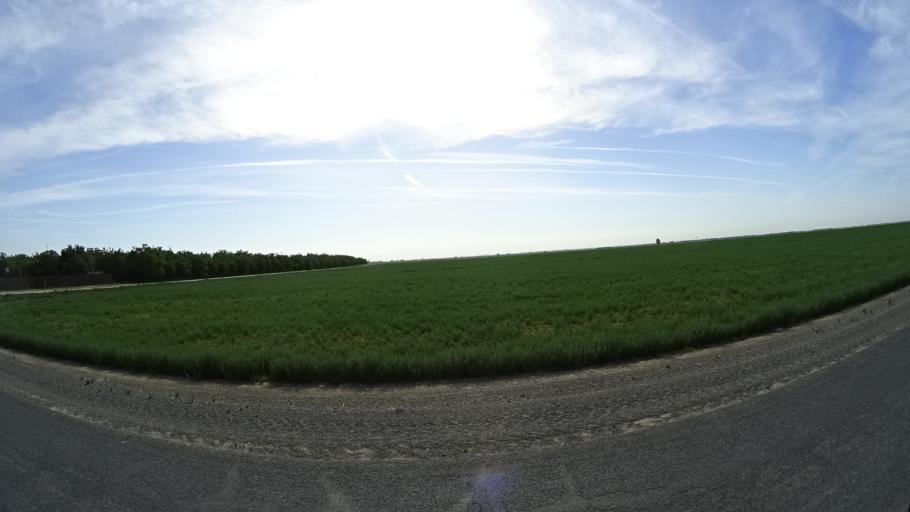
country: US
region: California
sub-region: Kings County
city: Hanford
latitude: 36.3681
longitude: -119.5470
